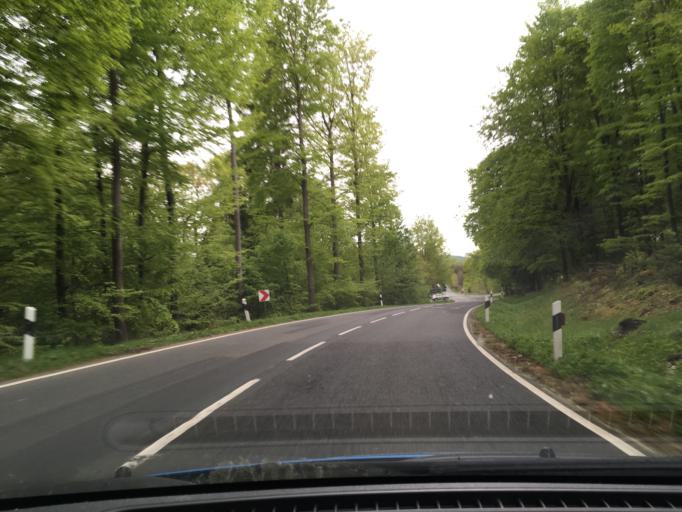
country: DE
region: Lower Saxony
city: Derental
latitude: 51.6875
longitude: 9.4541
